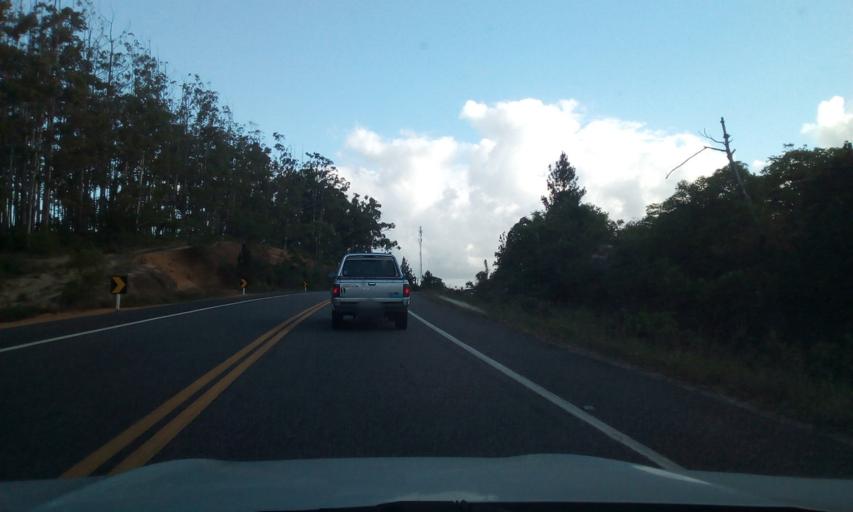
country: BR
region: Bahia
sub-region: Entre Rios
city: Entre Rios
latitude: -12.3072
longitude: -37.9040
